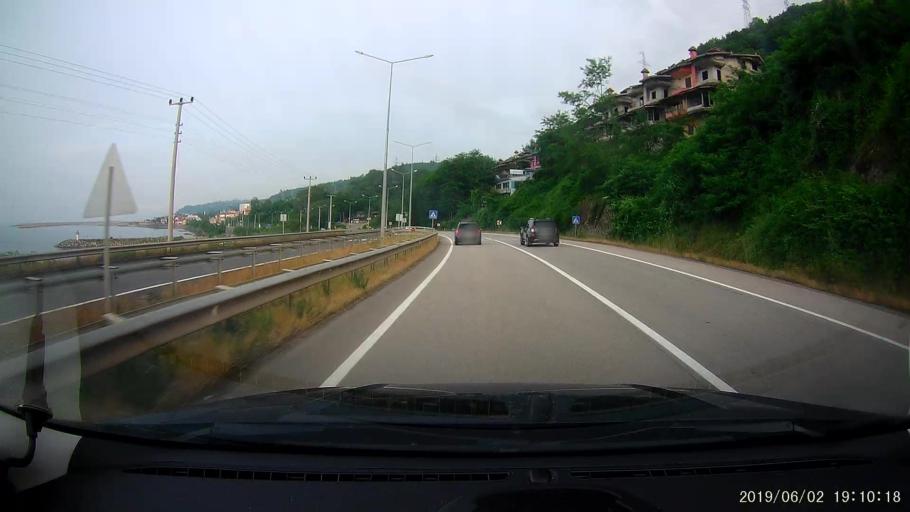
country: TR
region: Ordu
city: Gulyali
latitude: 40.9700
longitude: 38.0423
